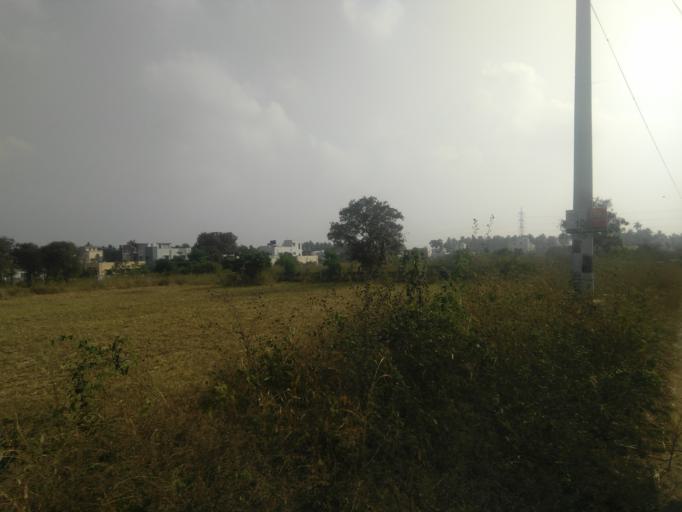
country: IN
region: Tamil Nadu
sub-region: Coimbatore
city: Periyanayakkanpalaiyam
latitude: 11.0784
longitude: 76.9299
